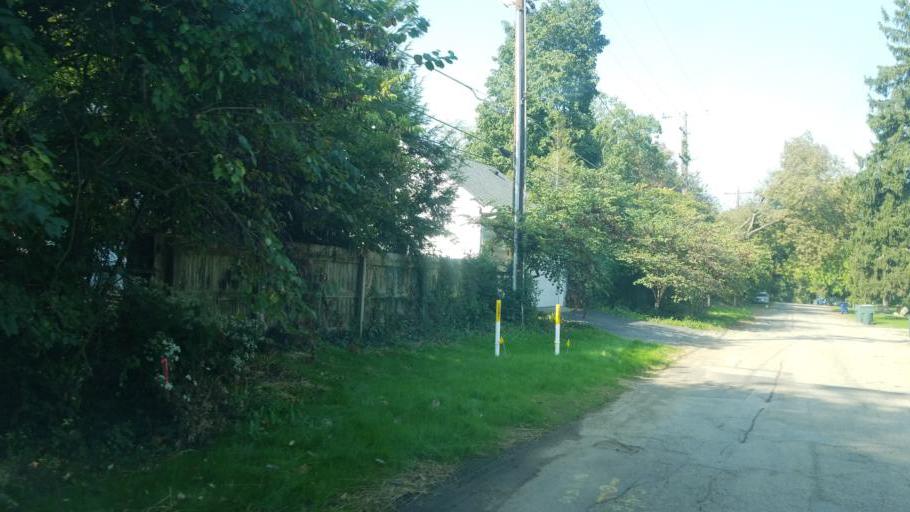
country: US
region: Ohio
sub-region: Franklin County
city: Worthington
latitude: 40.0626
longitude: -83.0213
